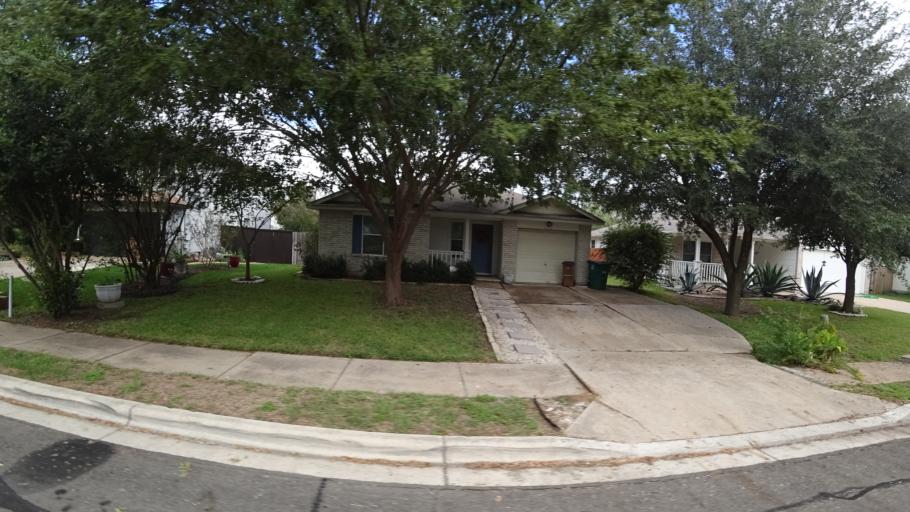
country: US
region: Texas
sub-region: Travis County
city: Onion Creek
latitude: 30.1545
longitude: -97.7385
